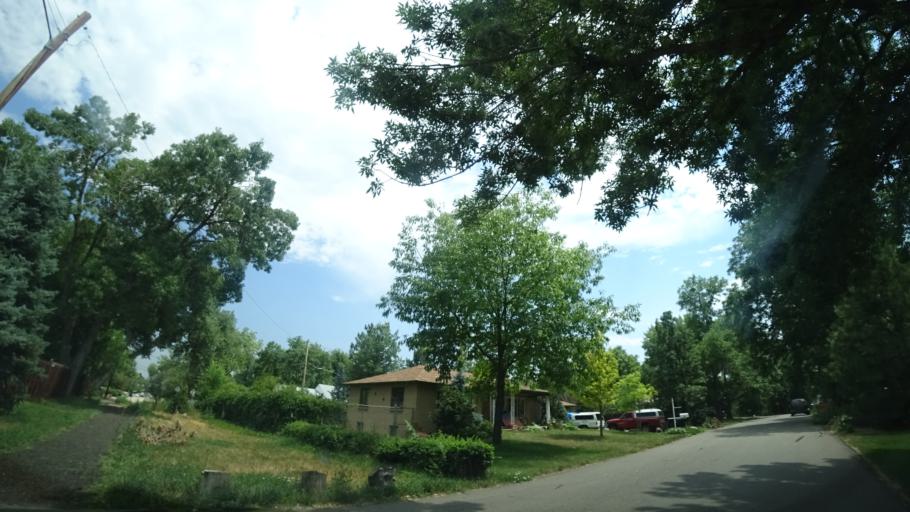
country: US
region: Colorado
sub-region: Jefferson County
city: Lakewood
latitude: 39.7202
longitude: -105.0846
